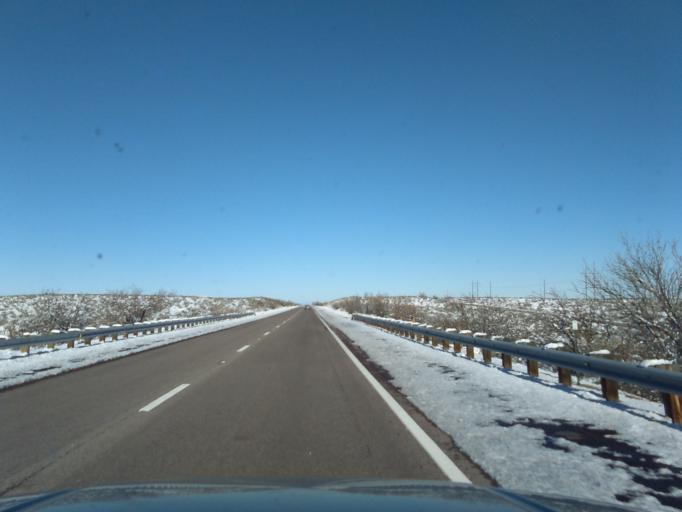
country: US
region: New Mexico
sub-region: Socorro County
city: Socorro
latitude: 33.6721
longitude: -107.0795
